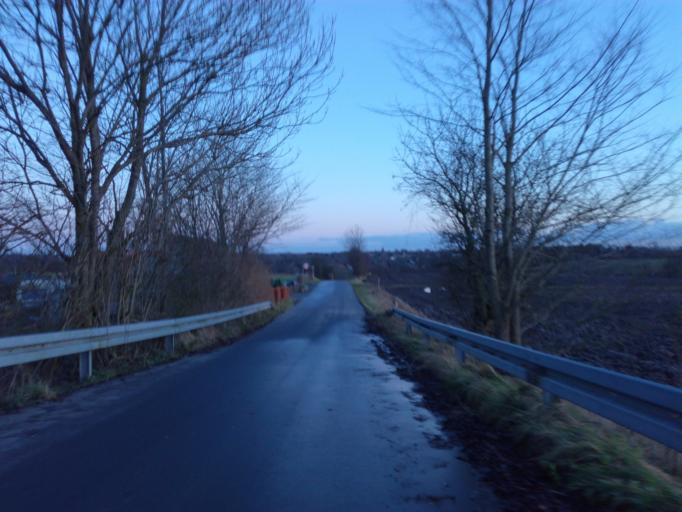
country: DK
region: South Denmark
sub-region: Fredericia Kommune
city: Snoghoj
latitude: 55.5538
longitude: 9.6828
